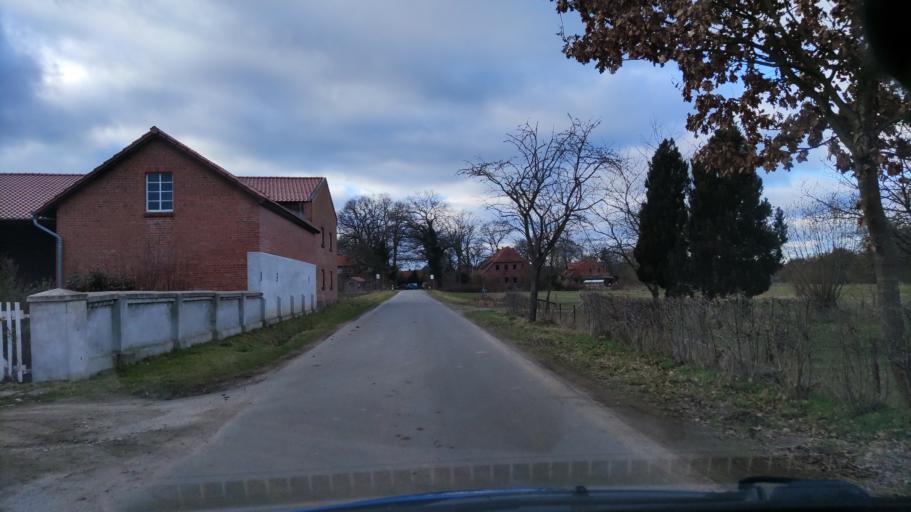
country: DE
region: Lower Saxony
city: Gohrde
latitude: 53.1570
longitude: 10.8830
